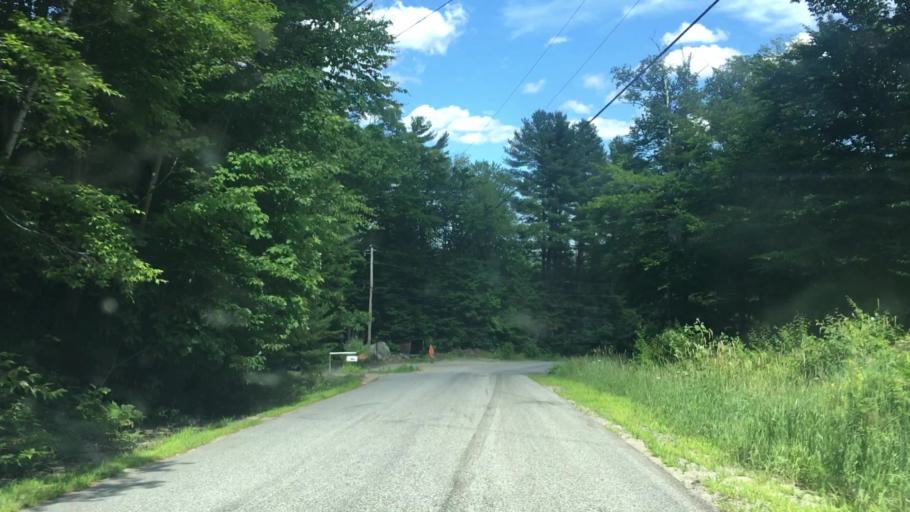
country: US
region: Maine
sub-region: Franklin County
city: Chesterville
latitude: 44.5621
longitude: -70.1346
